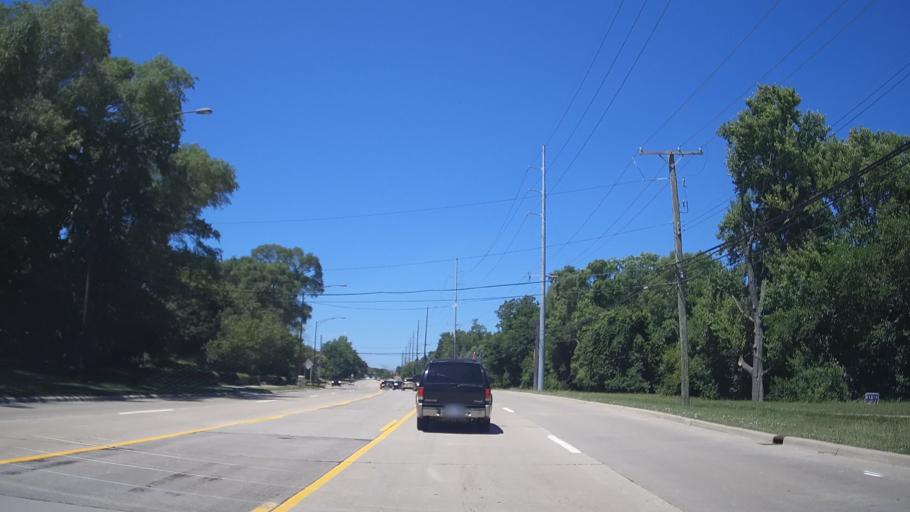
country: US
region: Michigan
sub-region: Oakland County
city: Troy
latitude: 42.5920
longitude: -83.1370
